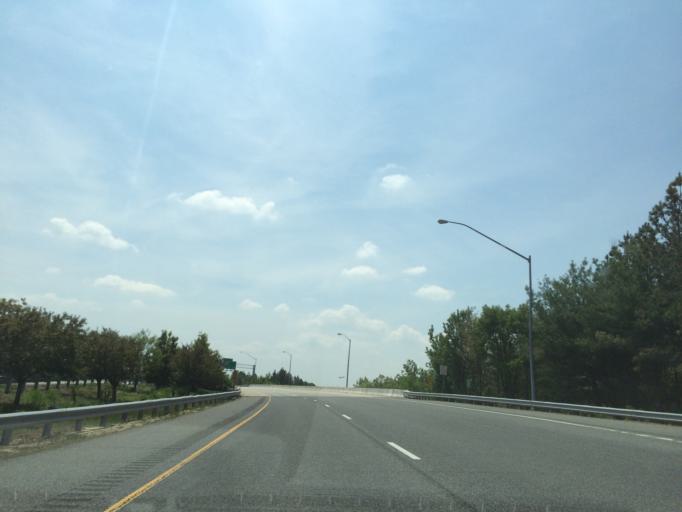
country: US
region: Maryland
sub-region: Howard County
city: Elkridge
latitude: 39.2023
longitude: -76.6959
